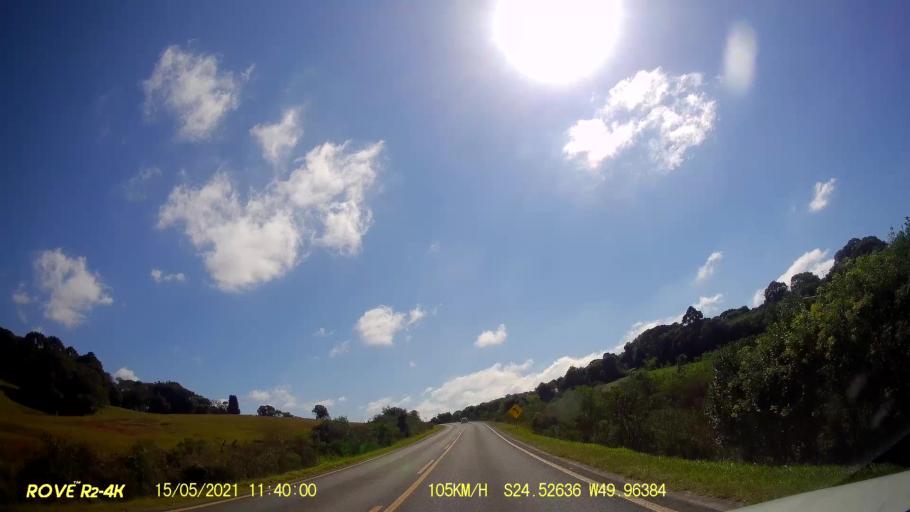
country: BR
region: Parana
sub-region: Pirai Do Sul
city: Pirai do Sul
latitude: -24.5269
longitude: -49.9638
